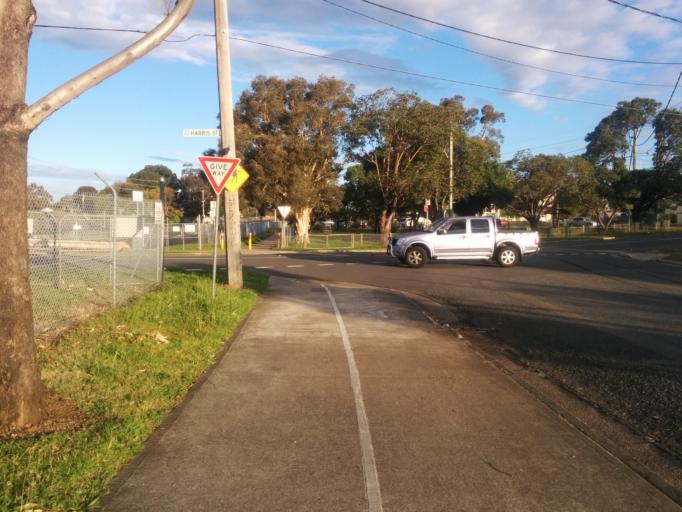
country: AU
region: New South Wales
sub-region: Holroyd
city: Guildford West
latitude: -33.8510
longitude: 150.9749
